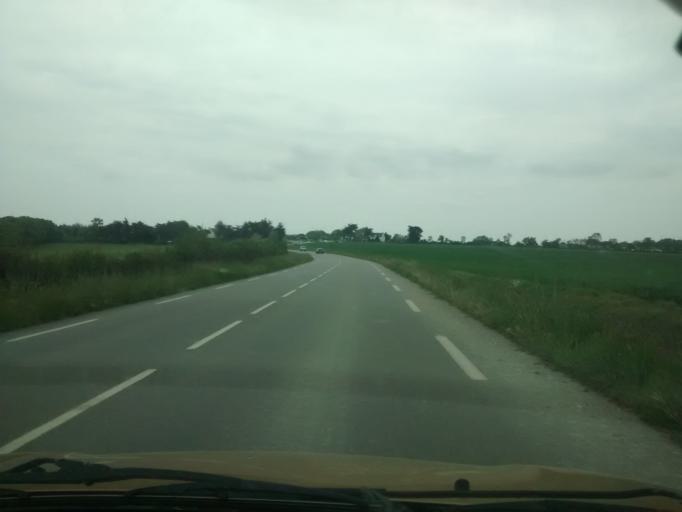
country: FR
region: Brittany
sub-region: Departement du Morbihan
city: Ambon
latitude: 47.5398
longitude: -2.5347
